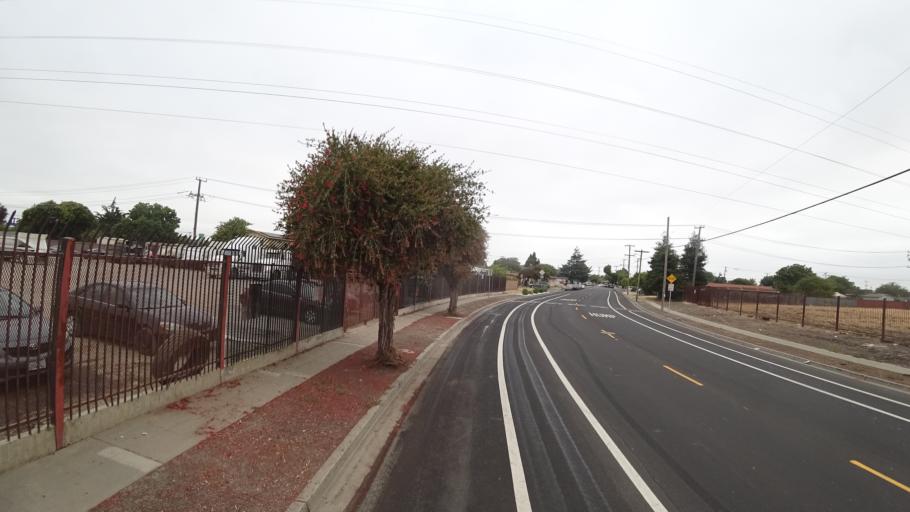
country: US
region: California
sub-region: Alameda County
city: Hayward
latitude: 37.6299
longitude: -122.1075
